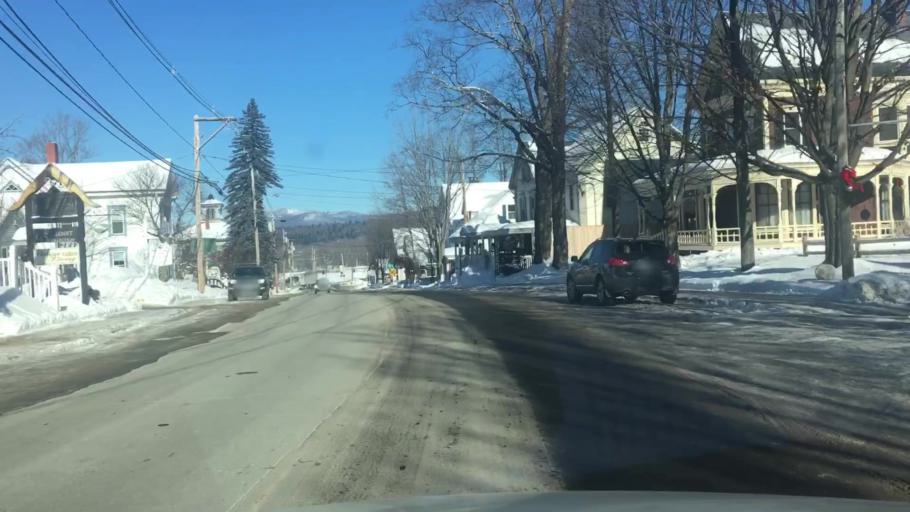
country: US
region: Maine
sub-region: Oxford County
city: Bethel
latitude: 44.4086
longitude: -70.7884
